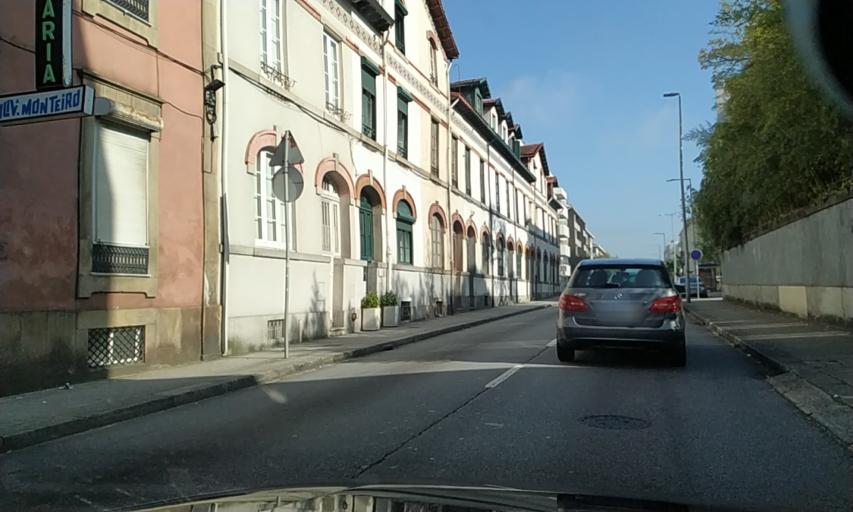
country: PT
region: Porto
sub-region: Porto
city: Porto
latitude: 41.1602
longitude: -8.6246
